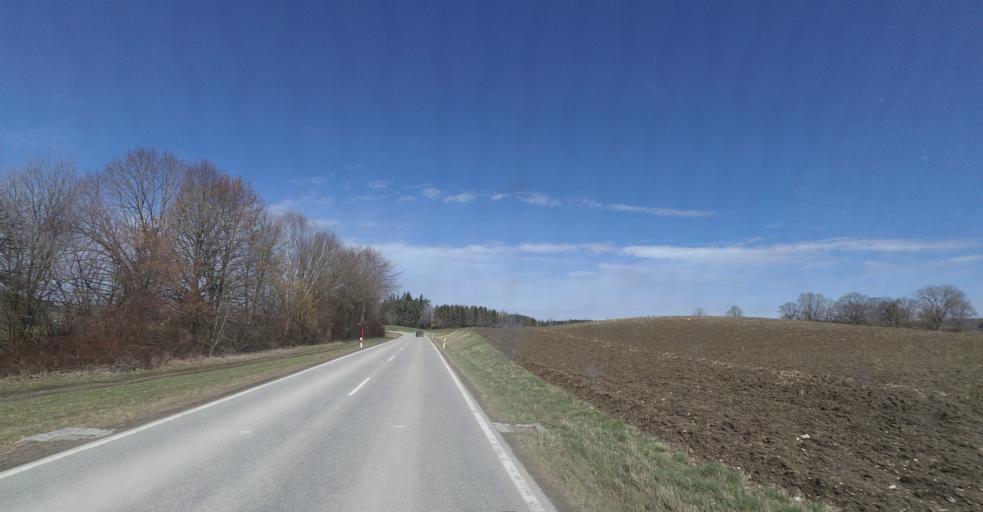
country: DE
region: Bavaria
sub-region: Upper Bavaria
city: Traunreut
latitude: 47.9379
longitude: 12.5534
